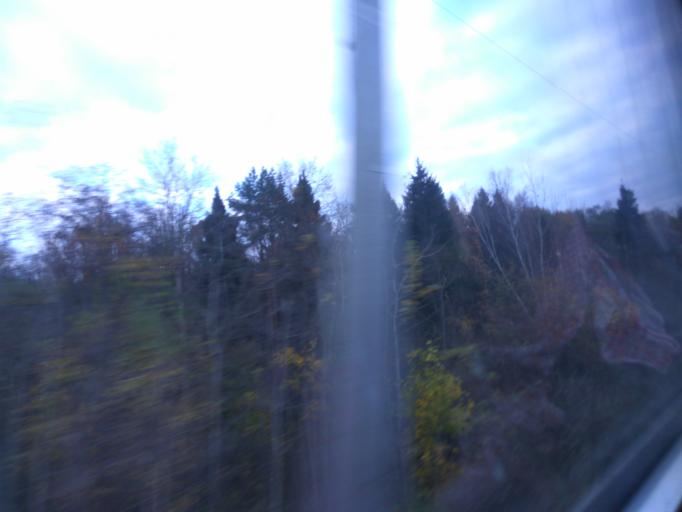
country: RU
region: Moskovskaya
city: Selyatino
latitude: 55.5327
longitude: 37.0035
